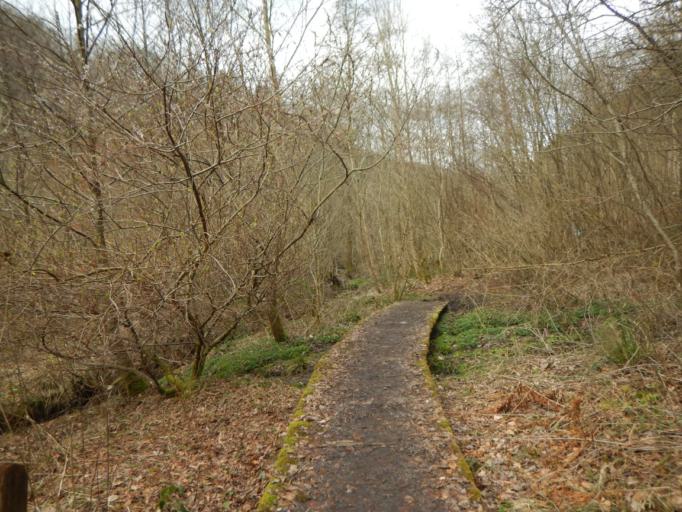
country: LU
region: Luxembourg
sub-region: Canton de Mersch
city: Tuntange
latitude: 49.7206
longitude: 6.0603
